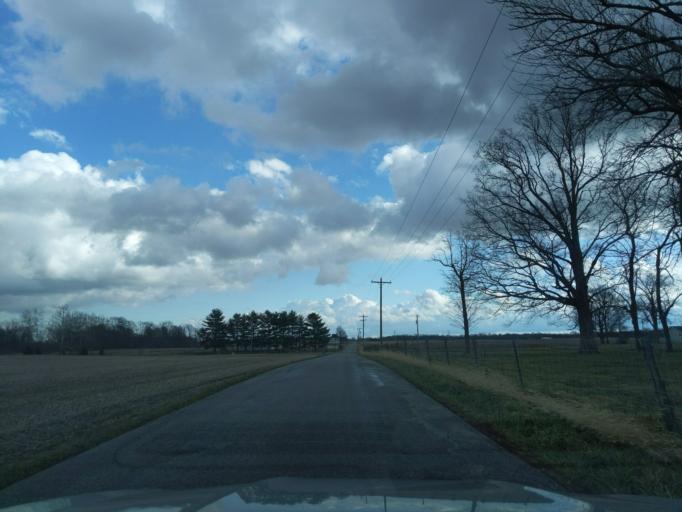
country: US
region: Indiana
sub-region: Decatur County
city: Saint Paul
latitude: 39.4092
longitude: -85.5469
